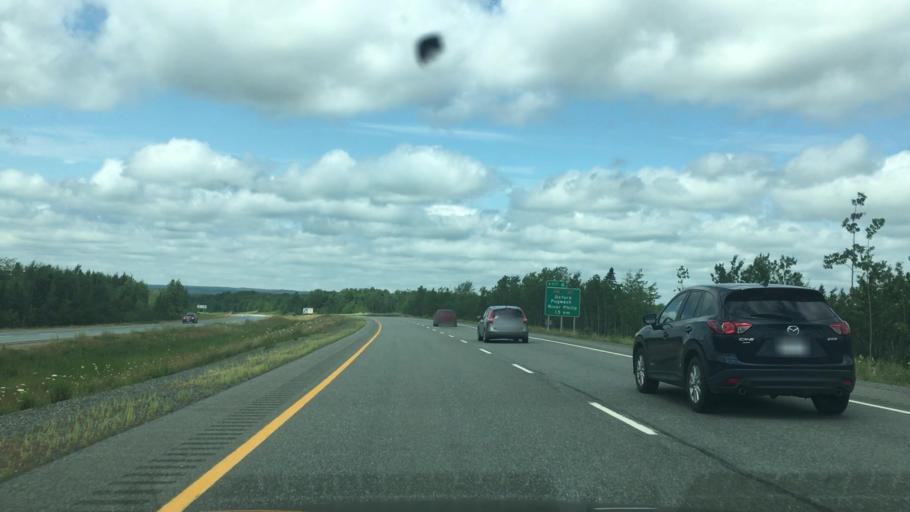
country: CA
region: Nova Scotia
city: Oxford
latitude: 45.7201
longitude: -63.8539
